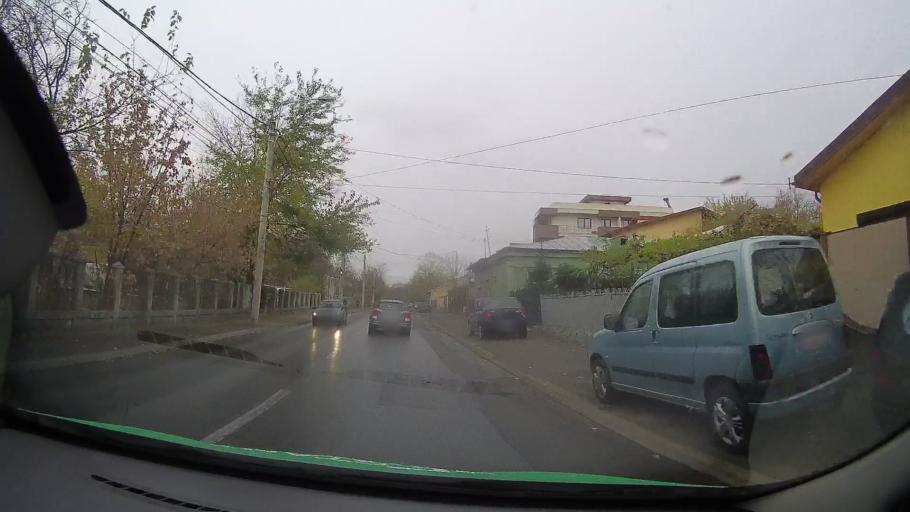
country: RO
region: Prahova
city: Ploiesti
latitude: 44.9338
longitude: 26.0058
